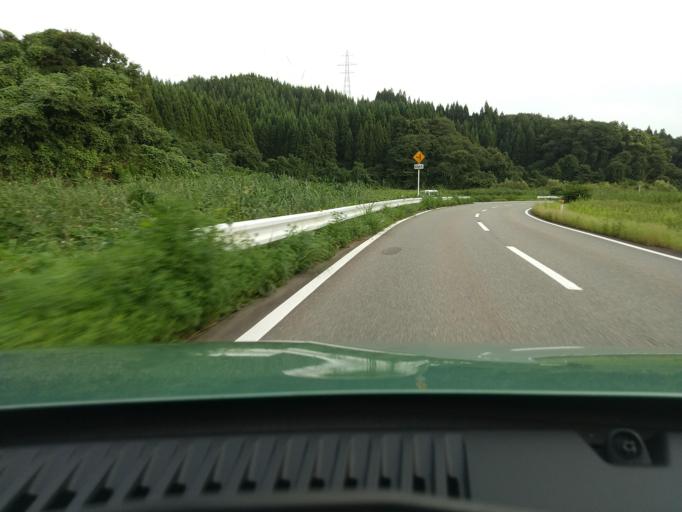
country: JP
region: Akita
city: Akita
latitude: 39.7483
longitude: 140.1612
